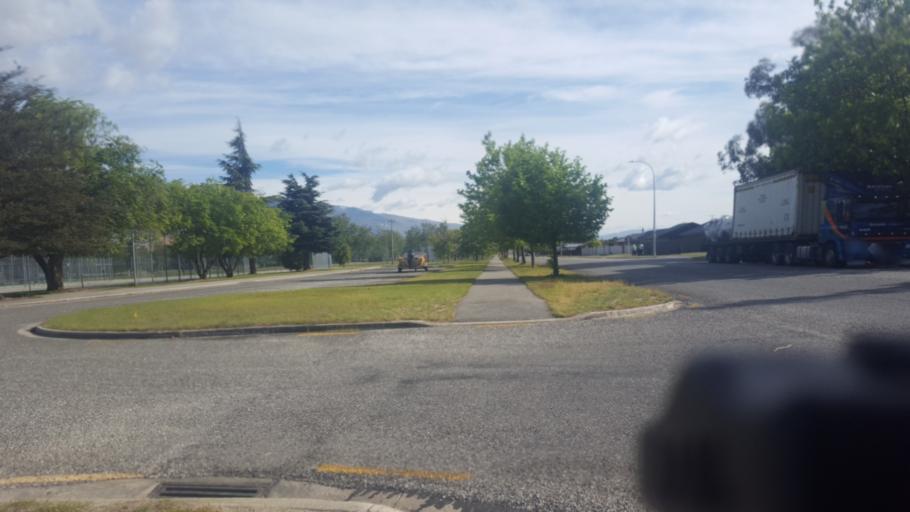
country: NZ
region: Otago
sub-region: Queenstown-Lakes District
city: Wanaka
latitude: -45.0435
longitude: 169.1963
